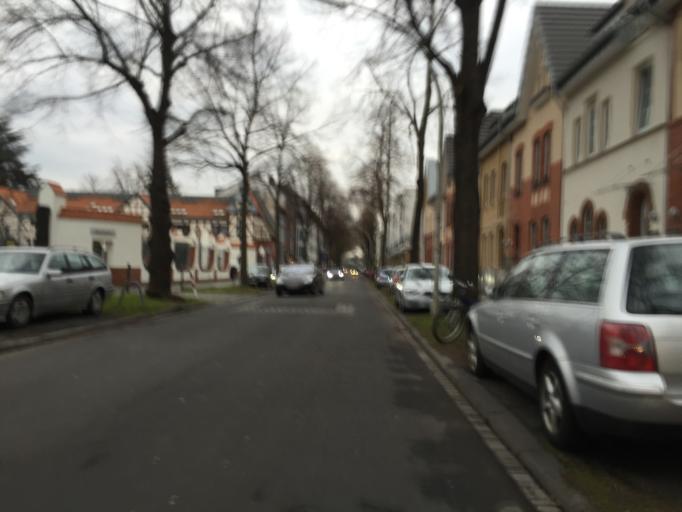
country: DE
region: North Rhine-Westphalia
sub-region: Regierungsbezirk Koln
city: Bonn
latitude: 50.7393
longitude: 7.0833
